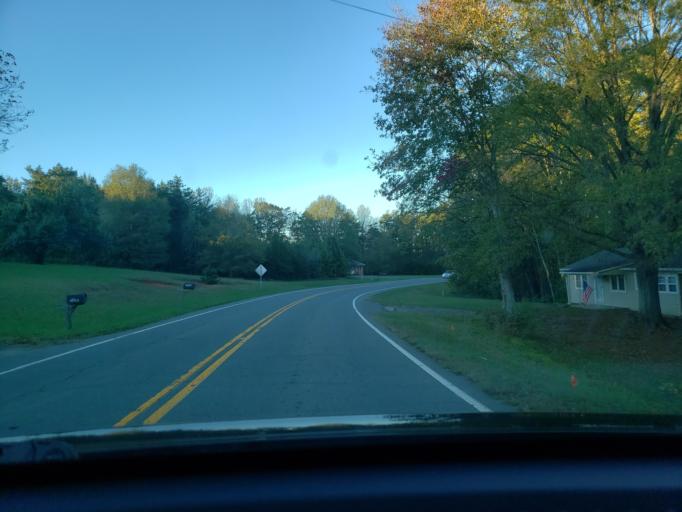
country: US
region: North Carolina
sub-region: Forsyth County
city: Rural Hall
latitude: 36.3137
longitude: -80.2382
